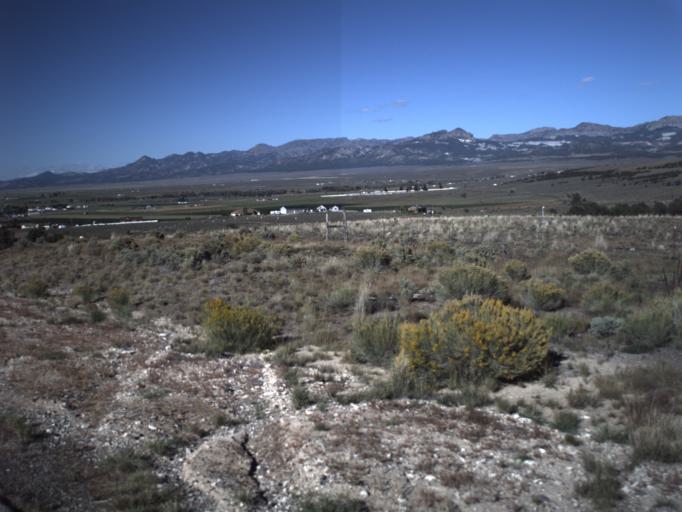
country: US
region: Utah
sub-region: Garfield County
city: Panguitch
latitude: 37.7990
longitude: -112.4374
